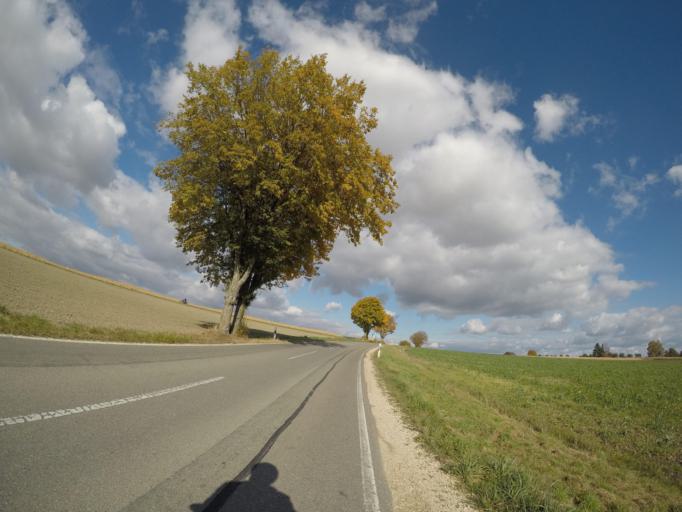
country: DE
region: Baden-Wuerttemberg
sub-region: Tuebingen Region
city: Oberstadion
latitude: 48.1790
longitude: 9.6895
